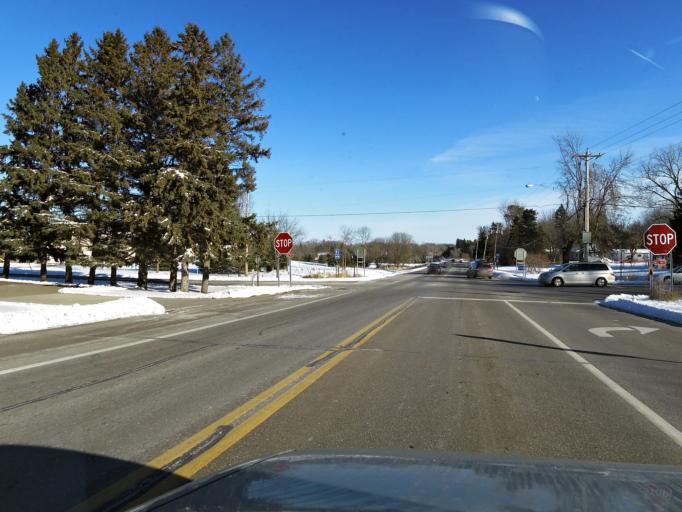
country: US
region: Minnesota
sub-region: Washington County
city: Oakdale
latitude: 44.9923
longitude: -92.9343
